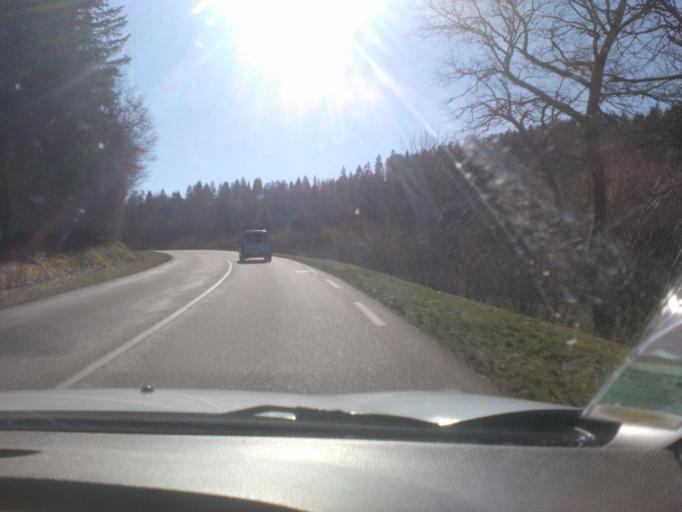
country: FR
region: Alsace
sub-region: Departement du Bas-Rhin
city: Rothau
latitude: 48.3819
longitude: 7.1411
